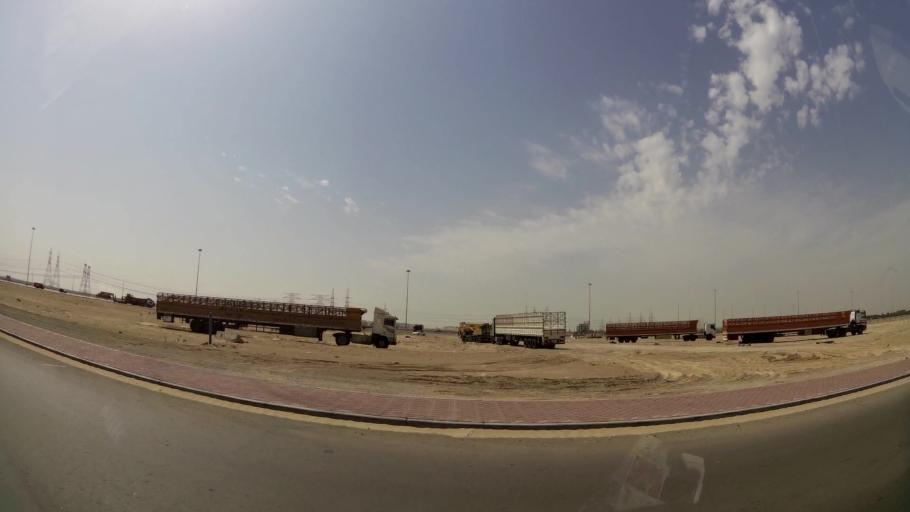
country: AE
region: Abu Dhabi
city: Abu Dhabi
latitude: 24.3100
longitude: 54.5306
